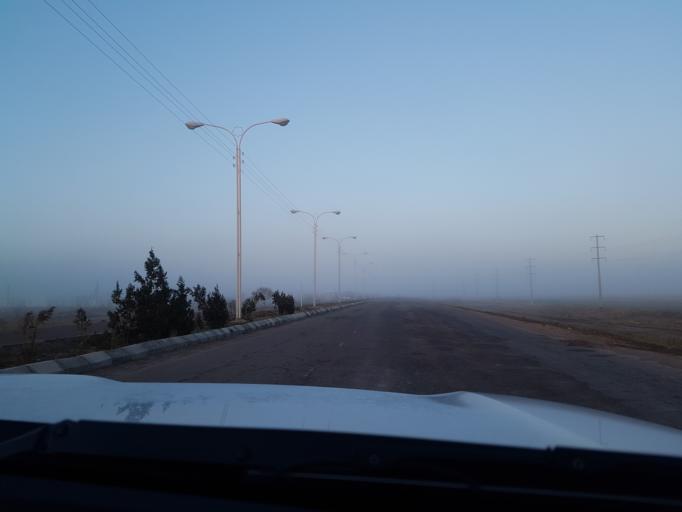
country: TM
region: Dasoguz
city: Koeneuergench
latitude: 41.7428
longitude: 58.7038
